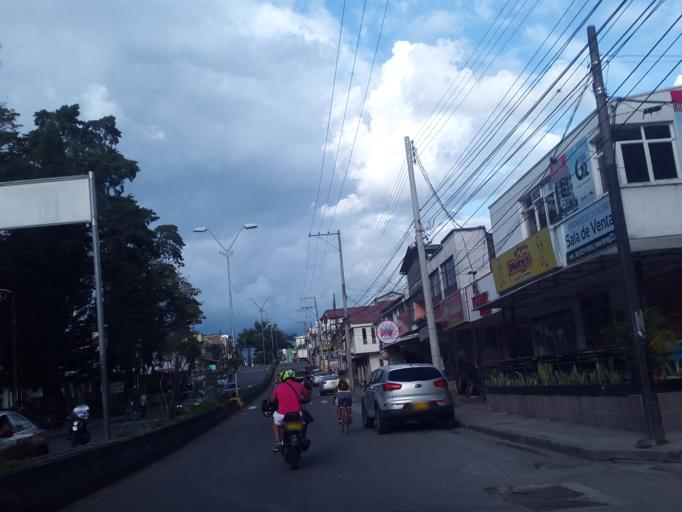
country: CO
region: Quindio
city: Armenia
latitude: 4.5422
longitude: -75.6726
